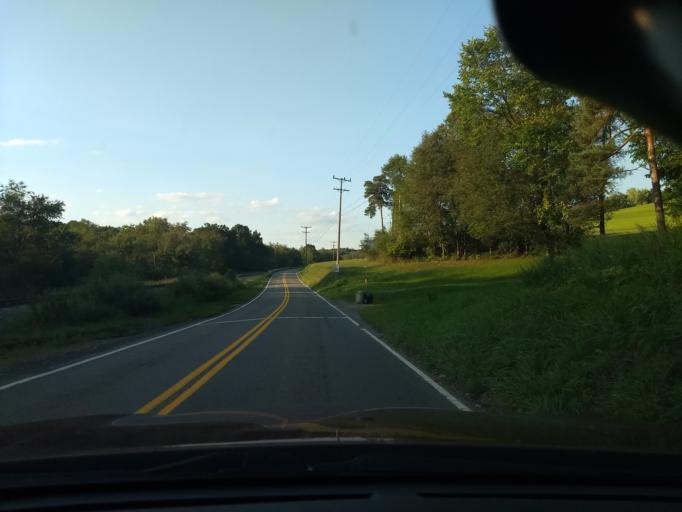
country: US
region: Pennsylvania
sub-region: Allegheny County
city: Gibsonia
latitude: 40.6370
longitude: -79.9709
